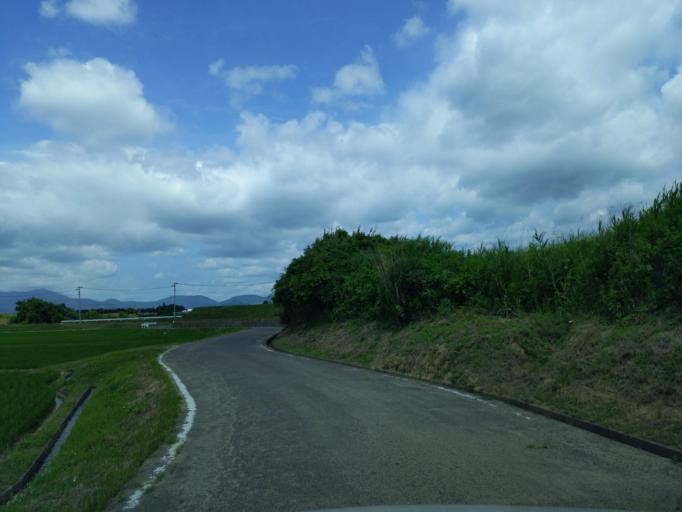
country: JP
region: Fukushima
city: Koriyama
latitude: 37.4393
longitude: 140.3566
